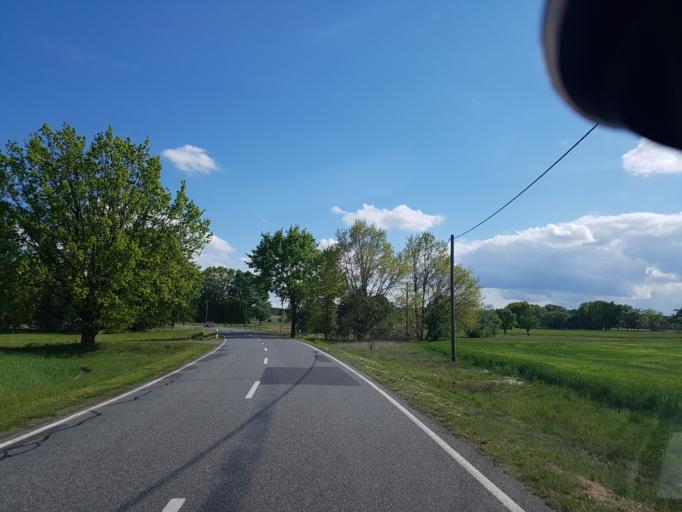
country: DE
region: Brandenburg
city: Drebkau
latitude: 51.6395
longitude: 14.2777
